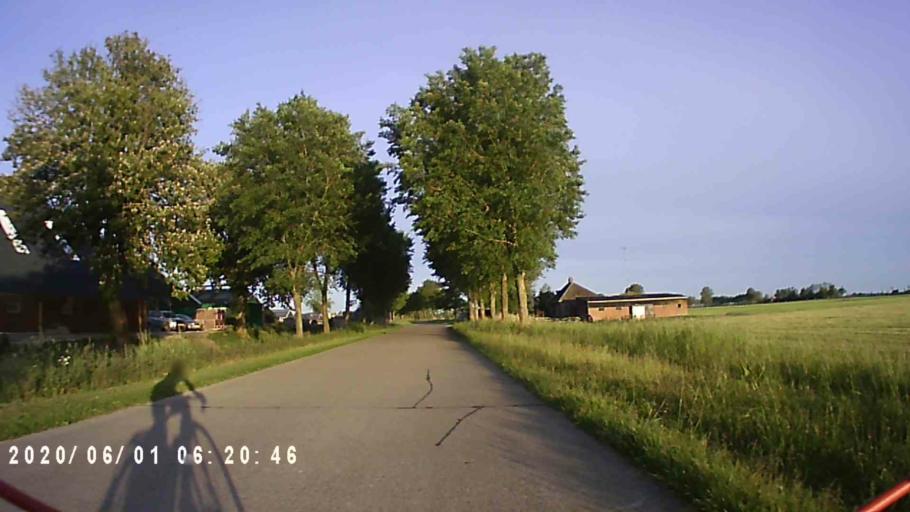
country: NL
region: Groningen
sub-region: Gemeente Grootegast
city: Grootegast
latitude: 53.2662
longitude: 6.2336
